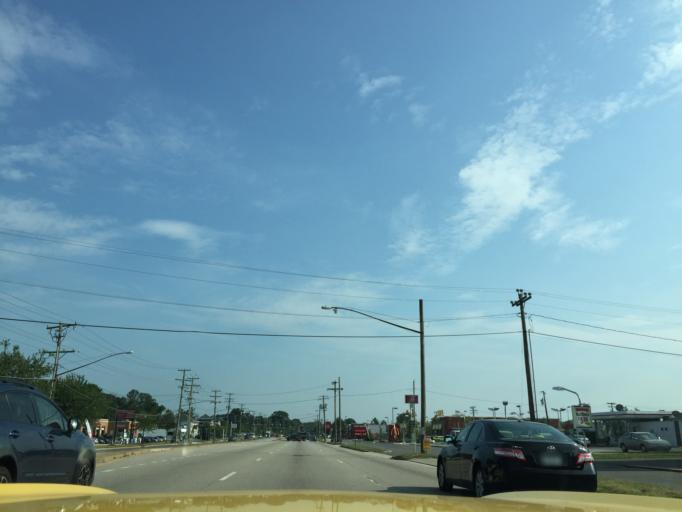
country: US
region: Virginia
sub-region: Fairfax County
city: Hybla Valley
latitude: 38.7526
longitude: -77.0834
